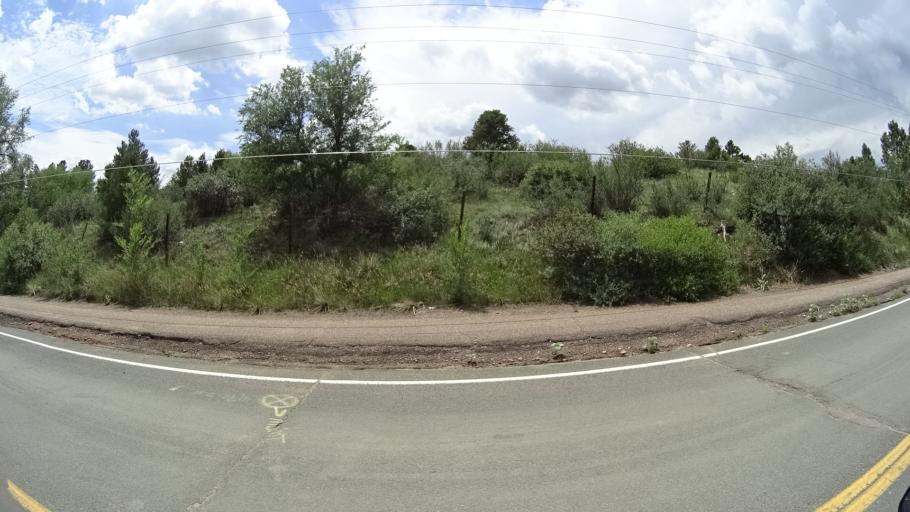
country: US
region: Colorado
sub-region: El Paso County
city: Colorado Springs
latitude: 38.8523
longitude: -104.8419
